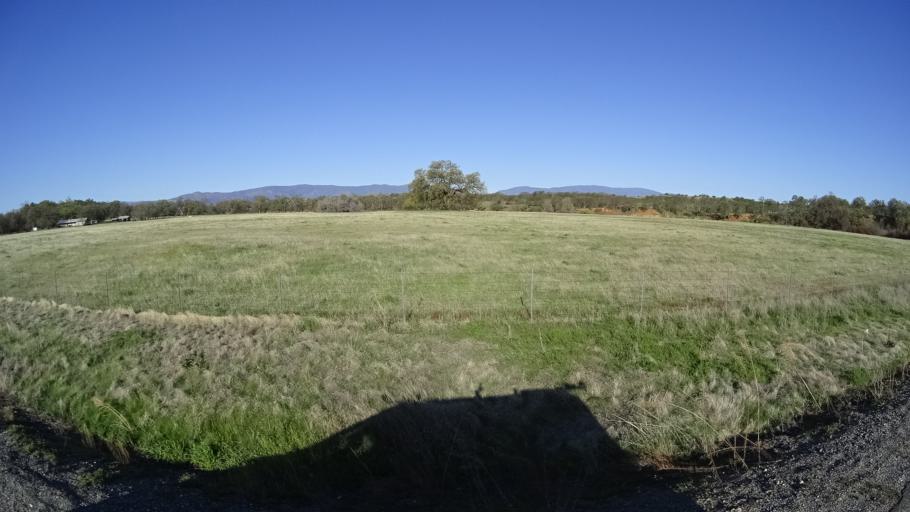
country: US
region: California
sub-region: Tehama County
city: Rancho Tehama Reserve
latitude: 39.8030
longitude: -122.4260
